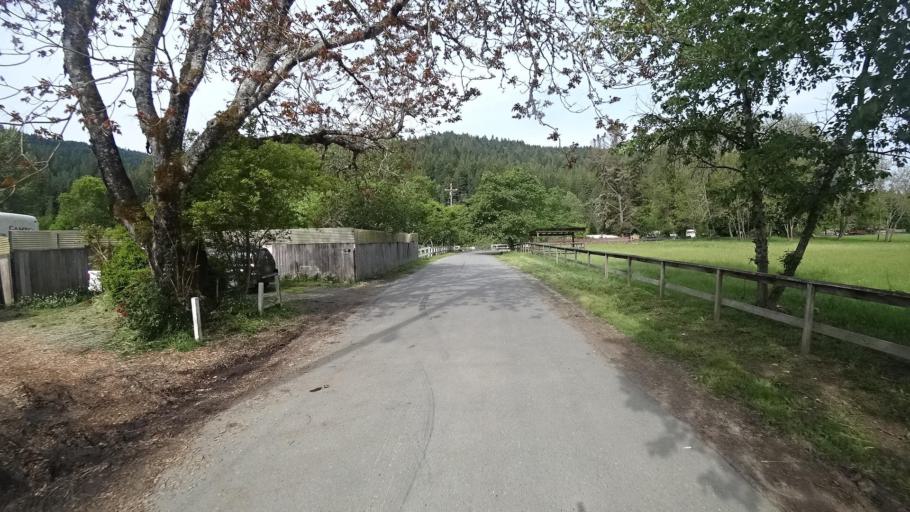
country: US
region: California
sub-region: Humboldt County
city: Redway
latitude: 40.2077
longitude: -123.7886
